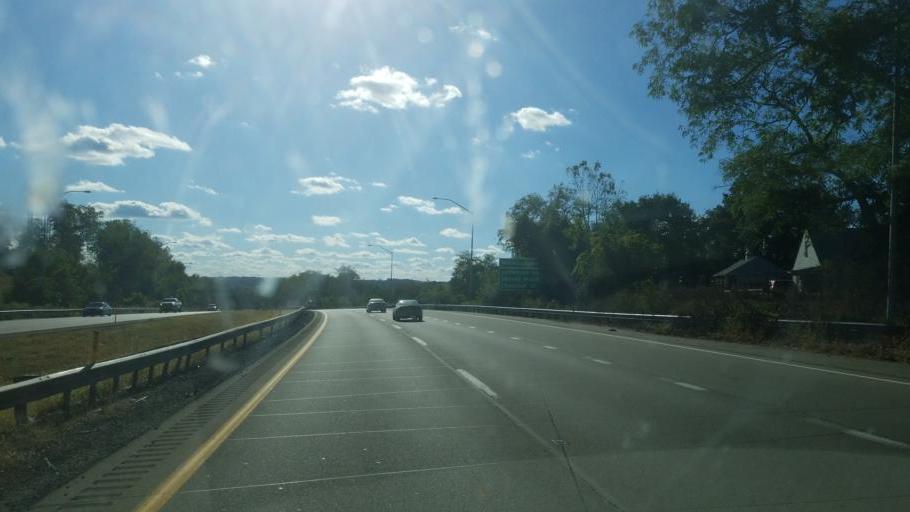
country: US
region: Pennsylvania
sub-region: Washington County
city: Washington
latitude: 40.1877
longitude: -80.2512
